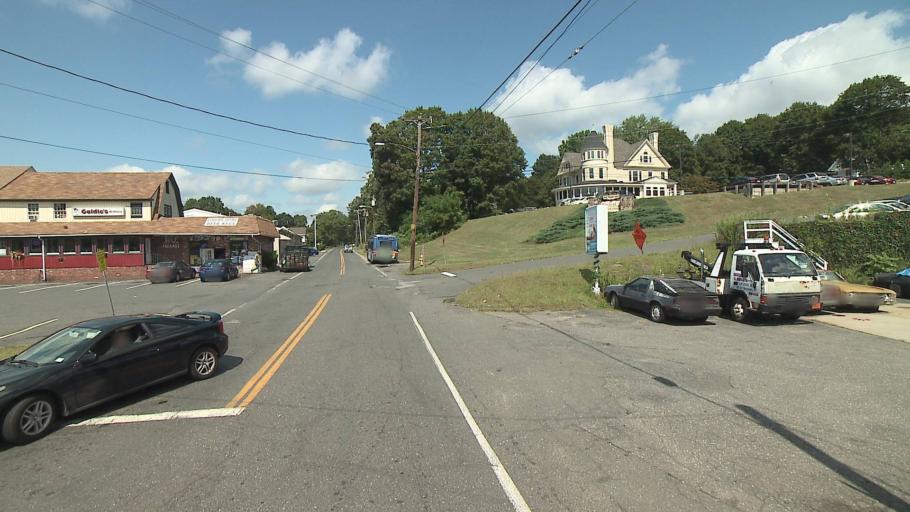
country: US
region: Connecticut
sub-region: New Haven County
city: Seymour
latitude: 41.3970
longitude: -73.0611
